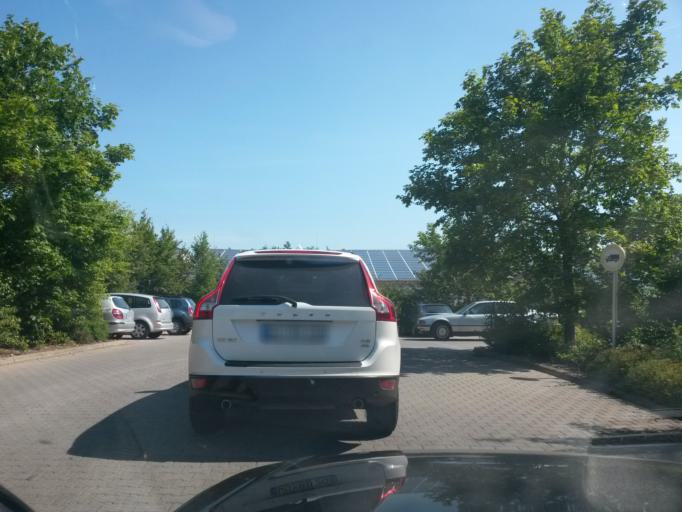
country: DE
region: Bavaria
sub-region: Regierungsbezirk Unterfranken
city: Estenfeld
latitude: 49.8412
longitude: 10.0178
